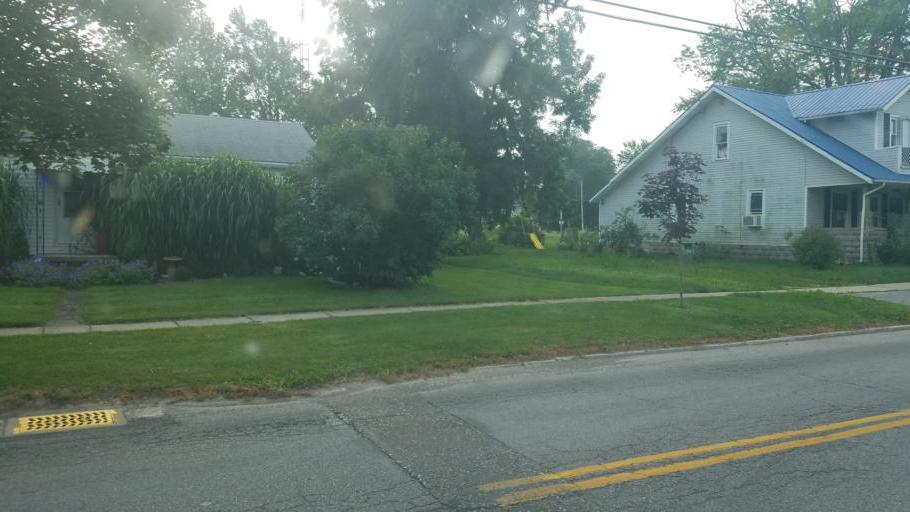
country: US
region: Ohio
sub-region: Morrow County
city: Cardington
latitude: 40.5036
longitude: -82.8956
